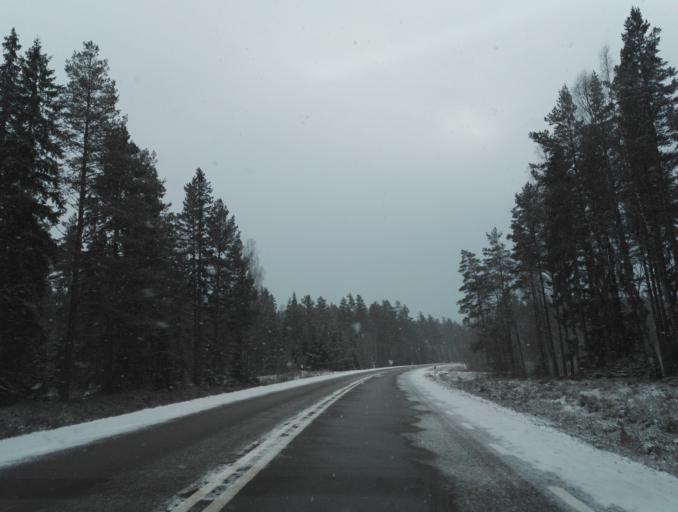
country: SE
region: Kronoberg
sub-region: Uppvidinge Kommun
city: Lenhovda
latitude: 56.9149
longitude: 15.3666
